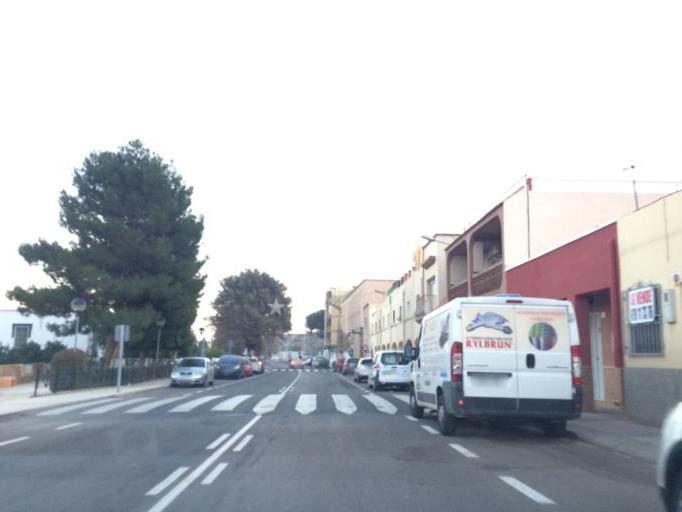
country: ES
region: Andalusia
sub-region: Provincia de Almeria
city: Gador
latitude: 36.9525
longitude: -2.4892
